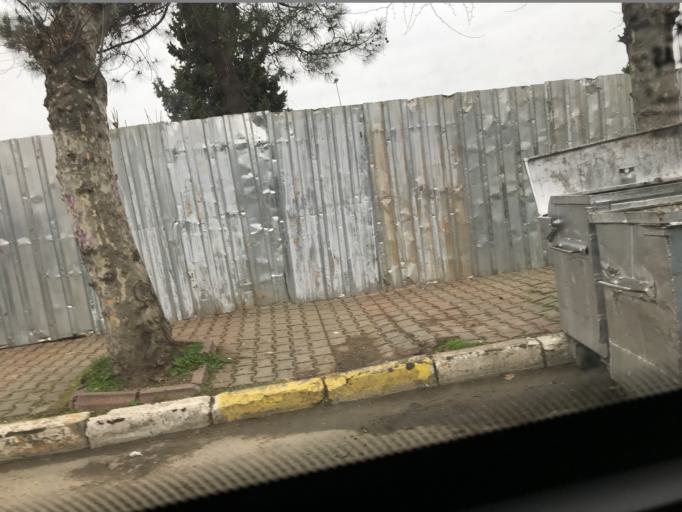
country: TR
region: Istanbul
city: Maltepe
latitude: 40.9224
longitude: 29.1274
